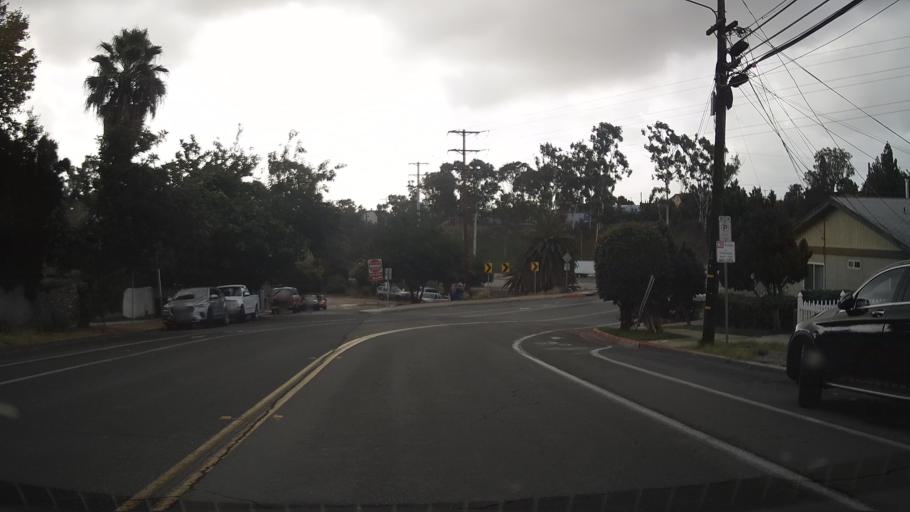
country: US
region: California
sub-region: San Diego County
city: San Diego
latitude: 32.7469
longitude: -117.1194
